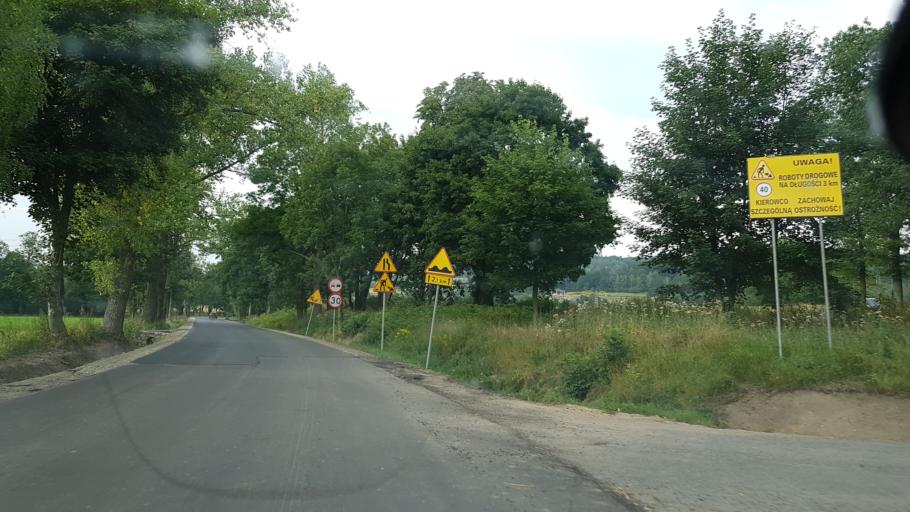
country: PL
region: Lower Silesian Voivodeship
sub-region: Powiat jeleniogorski
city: Janowice Wielkie
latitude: 50.8865
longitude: 15.9221
